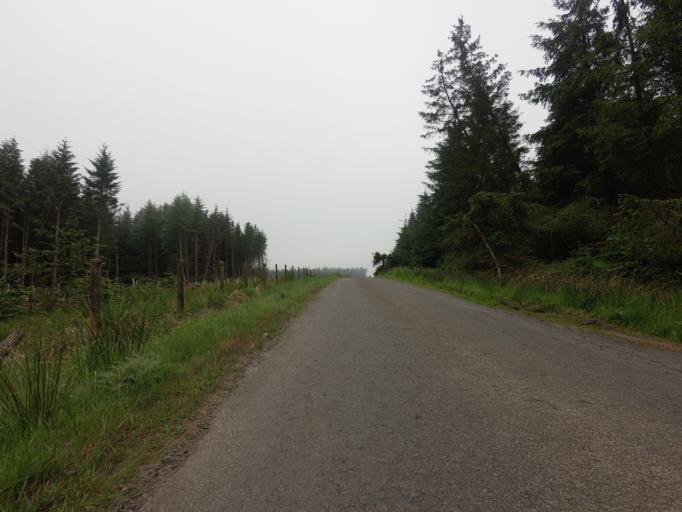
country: GB
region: Scotland
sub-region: Fife
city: Townhill
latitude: 56.1455
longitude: -3.4511
